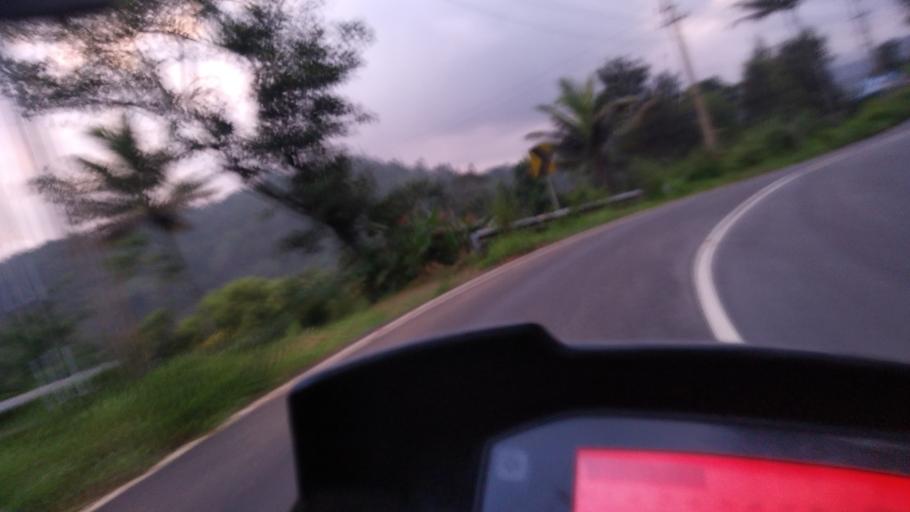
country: IN
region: Kerala
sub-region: Idukki
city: Munnar
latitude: 9.9666
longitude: 77.1097
